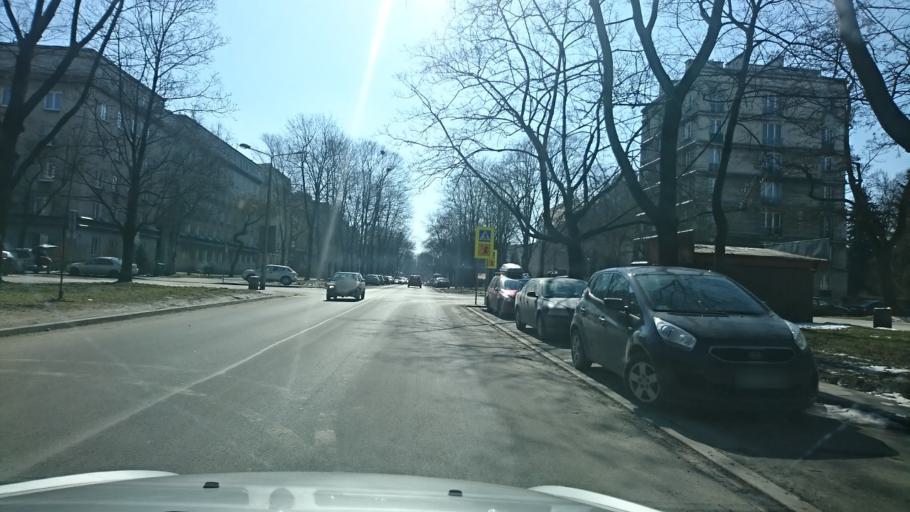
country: PL
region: Lesser Poland Voivodeship
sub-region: Powiat wielicki
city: Kokotow
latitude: 50.0773
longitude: 20.0453
